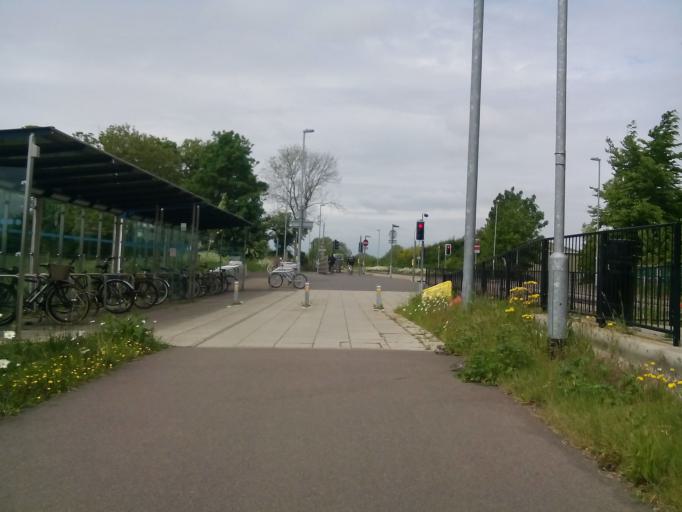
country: GB
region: England
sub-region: Cambridgeshire
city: Swavesey
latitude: 52.3061
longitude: 0.0001
